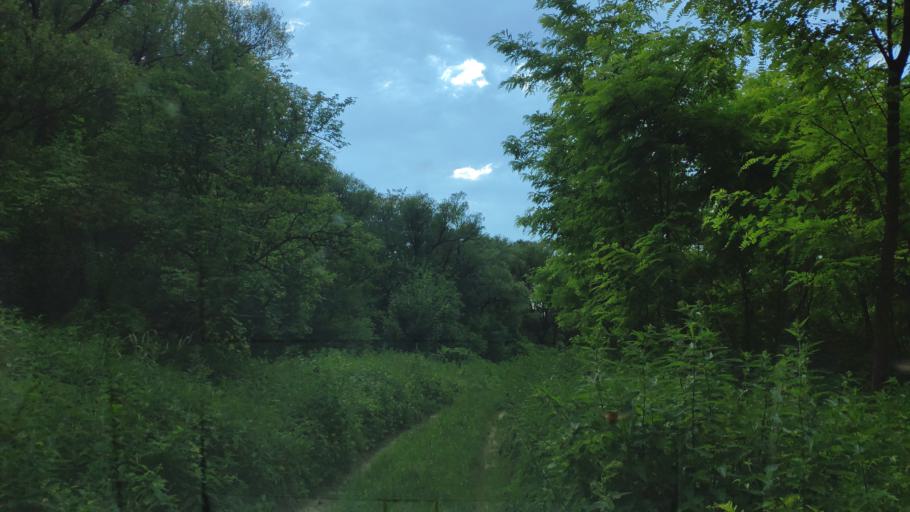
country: SK
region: Banskobystricky
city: Rimavska Sobota
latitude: 48.2567
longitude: 20.1169
